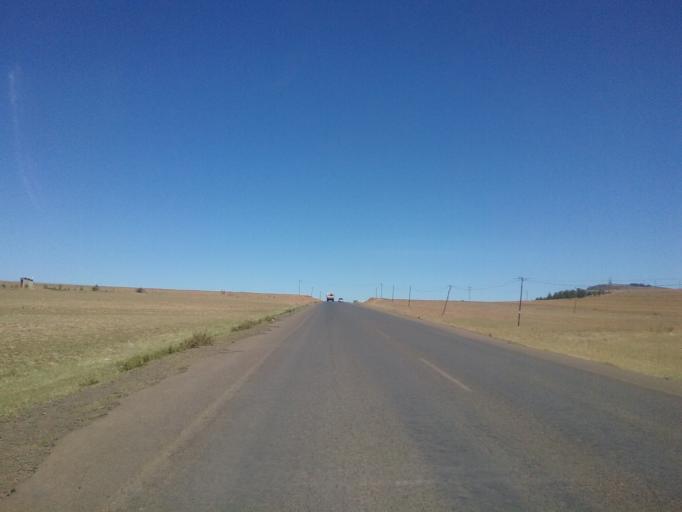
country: LS
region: Quthing
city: Quthing
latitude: -30.3938
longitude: 27.6350
